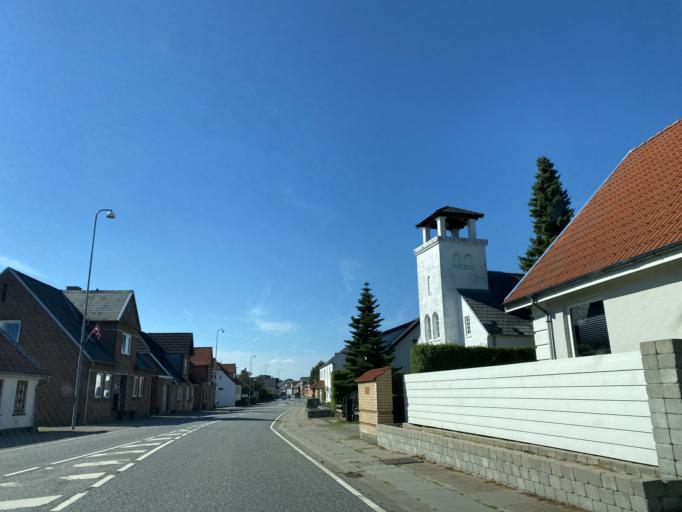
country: DK
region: Central Jutland
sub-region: Hedensted Kommune
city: Torring
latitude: 55.8600
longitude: 9.4184
